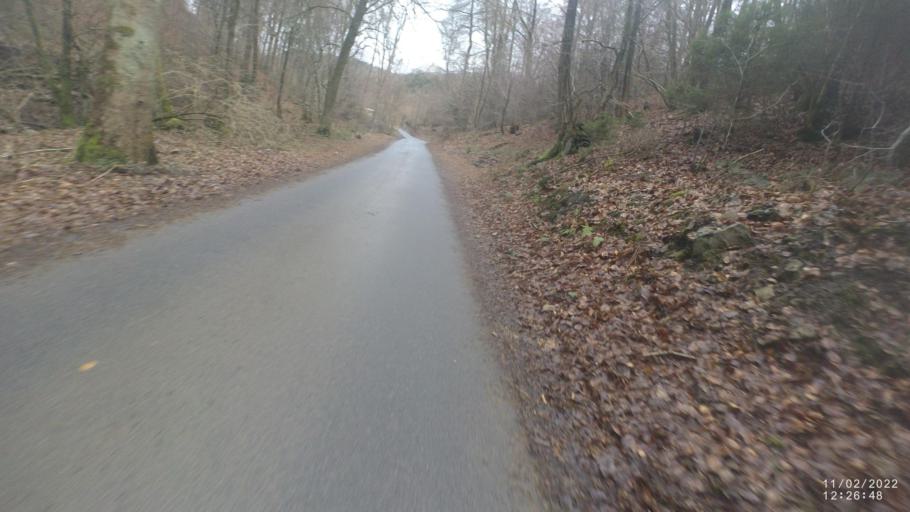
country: DE
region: North Rhine-Westphalia
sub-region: Regierungsbezirk Arnsberg
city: Nachrodt-Wiblingwerde
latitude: 51.3163
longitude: 7.6328
